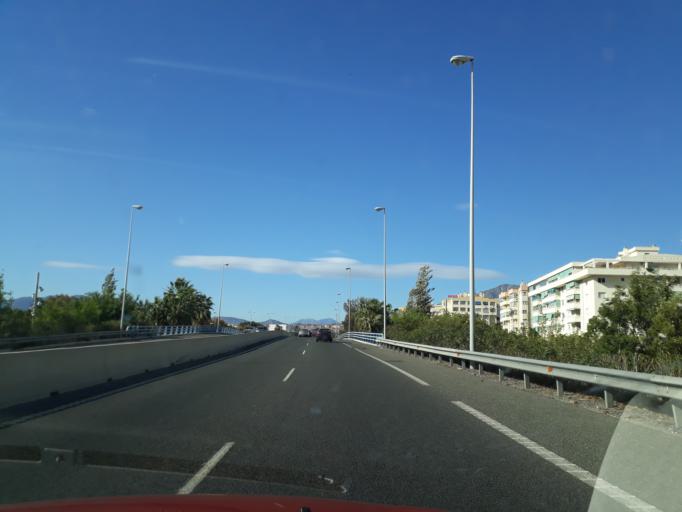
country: ES
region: Andalusia
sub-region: Provincia de Malaga
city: Fuengirola
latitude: 36.5307
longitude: -4.6295
